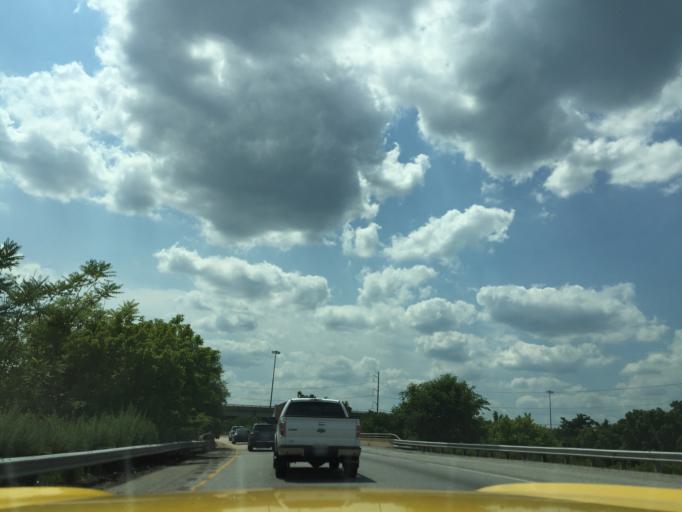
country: US
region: Pennsylvania
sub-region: Delaware County
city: Woodlyn
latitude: 39.8682
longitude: -75.3408
